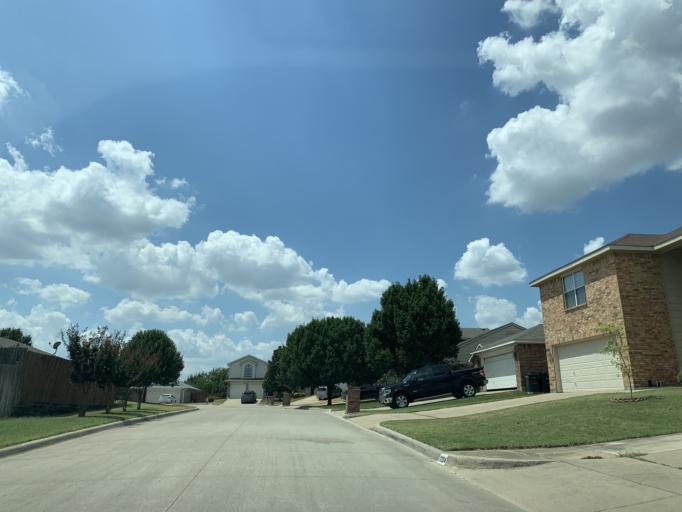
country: US
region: Texas
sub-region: Tarrant County
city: White Settlement
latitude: 32.7329
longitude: -97.5046
